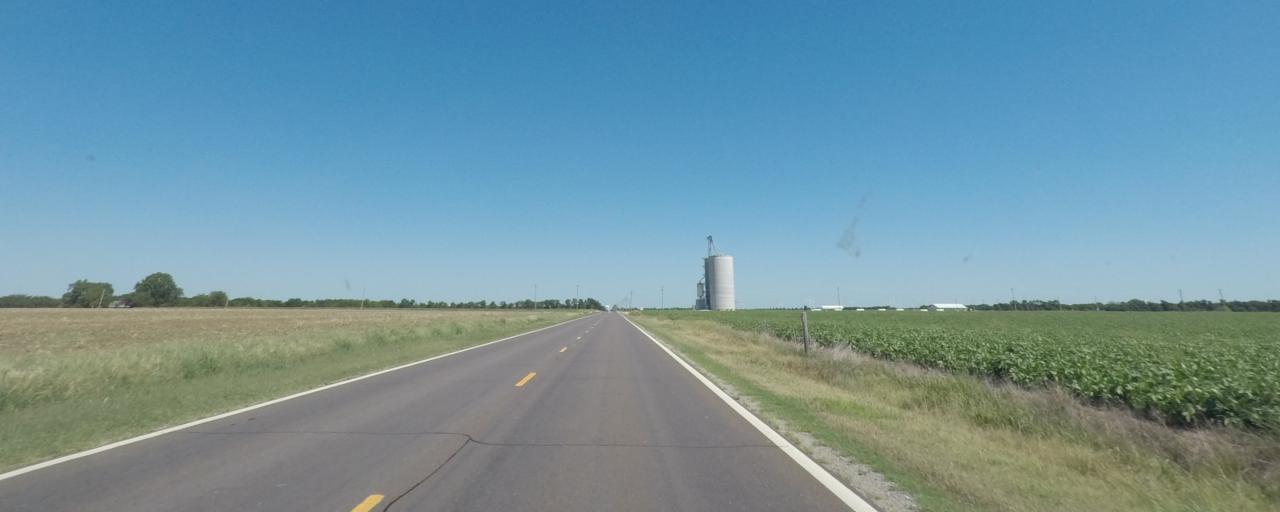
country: US
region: Kansas
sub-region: Sumner County
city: Wellington
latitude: 37.0829
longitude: -97.4014
